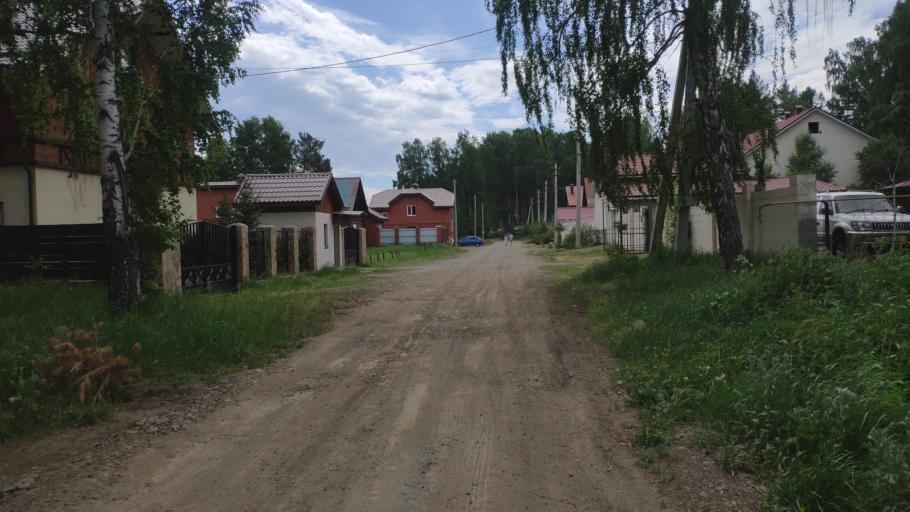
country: RU
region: Bashkortostan
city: Abzakovo
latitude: 53.8139
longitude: 58.6347
